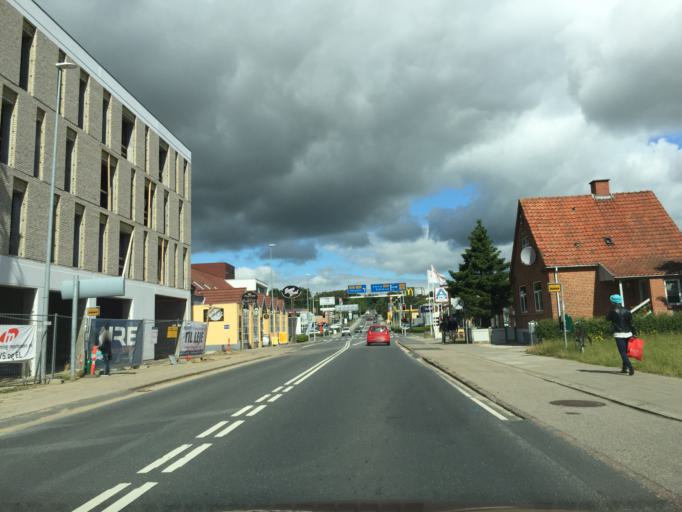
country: DK
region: Central Jutland
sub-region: Silkeborg Kommune
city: Silkeborg
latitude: 56.1833
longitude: 9.5461
